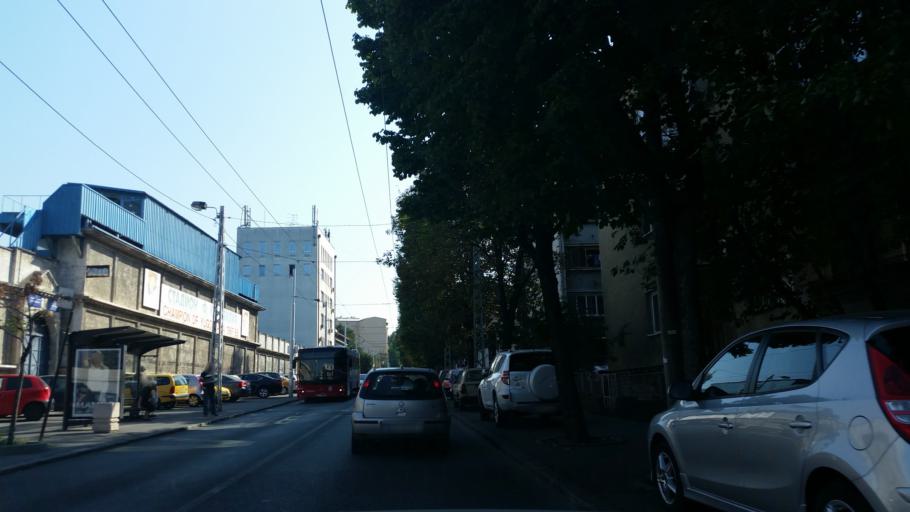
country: RS
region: Central Serbia
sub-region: Belgrade
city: Vracar
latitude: 44.7909
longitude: 20.4941
